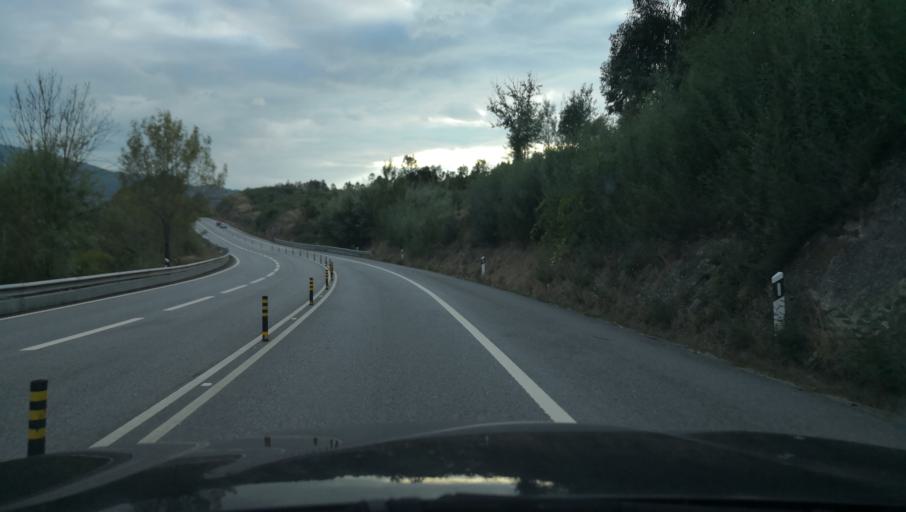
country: PT
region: Porto
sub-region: Amarante
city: Amarante
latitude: 41.2712
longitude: -8.0147
